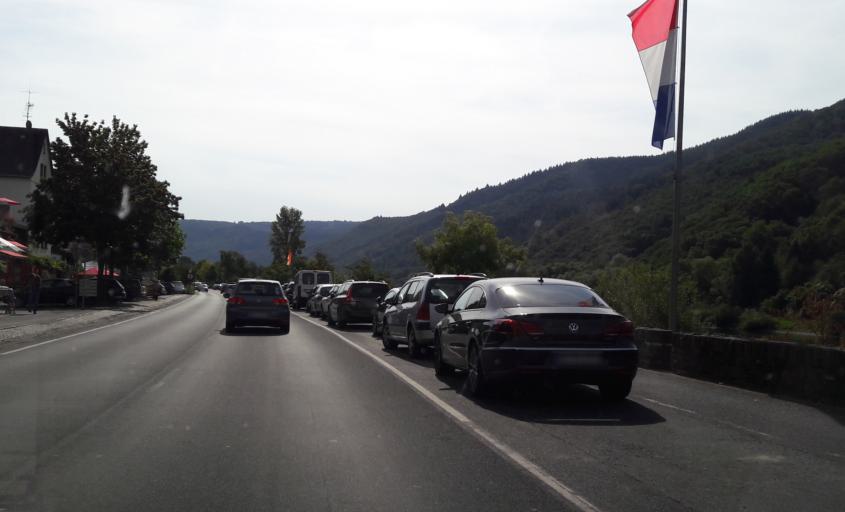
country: DE
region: Rheinland-Pfalz
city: Ediger-Eller
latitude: 50.0947
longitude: 7.1563
